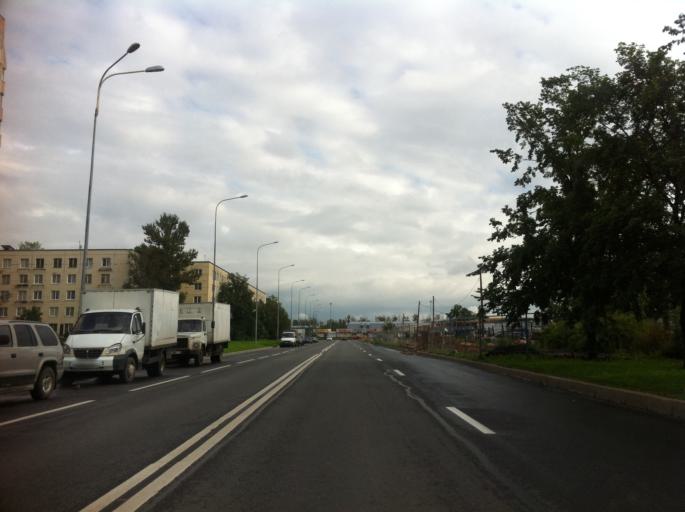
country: RU
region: St.-Petersburg
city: Dachnoye
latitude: 59.8338
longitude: 30.2490
